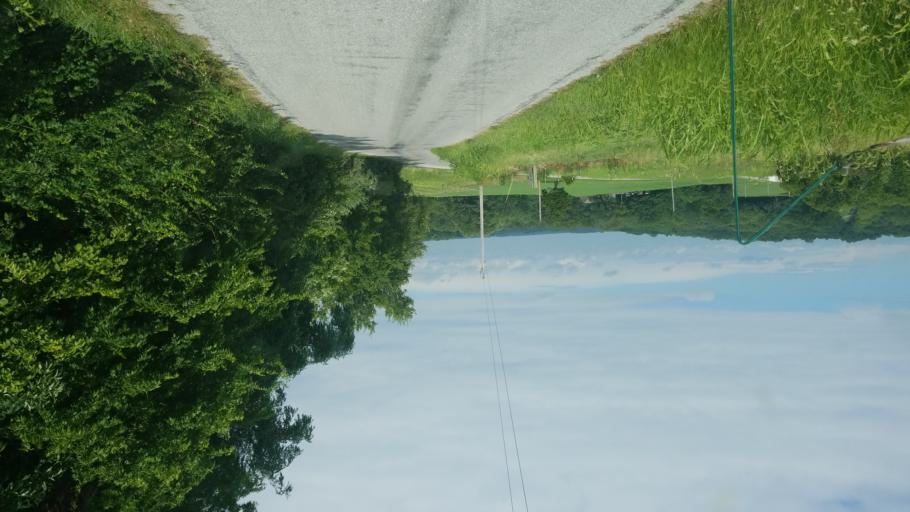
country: US
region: Illinois
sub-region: Union County
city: Cobden
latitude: 37.6034
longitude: -89.3670
